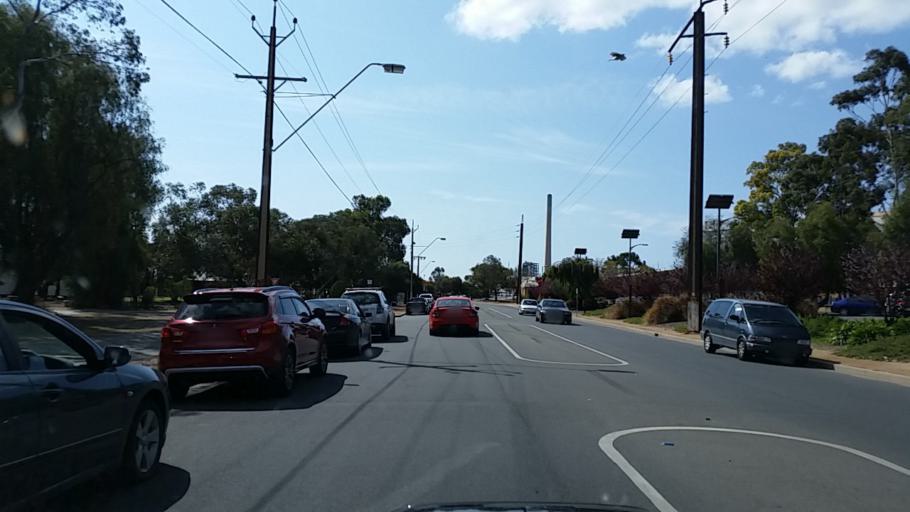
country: AU
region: South Australia
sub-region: Port Pirie City and Dists
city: Port Pirie
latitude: -33.1830
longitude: 138.0113
